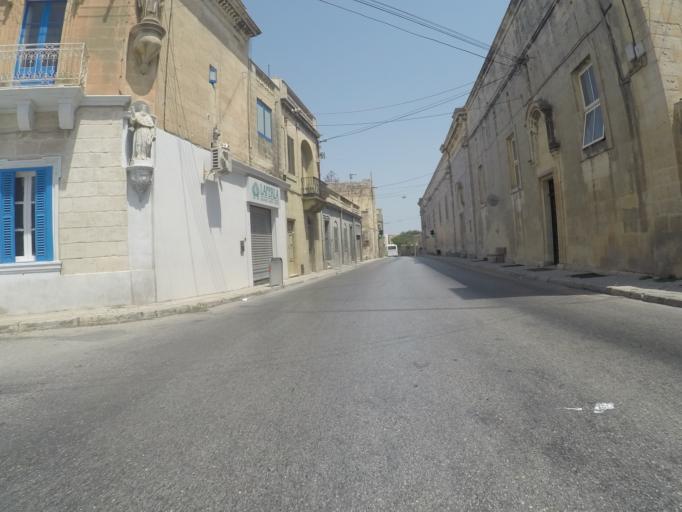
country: MT
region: Ir-Rabat
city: Rabat
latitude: 35.8808
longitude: 14.4013
